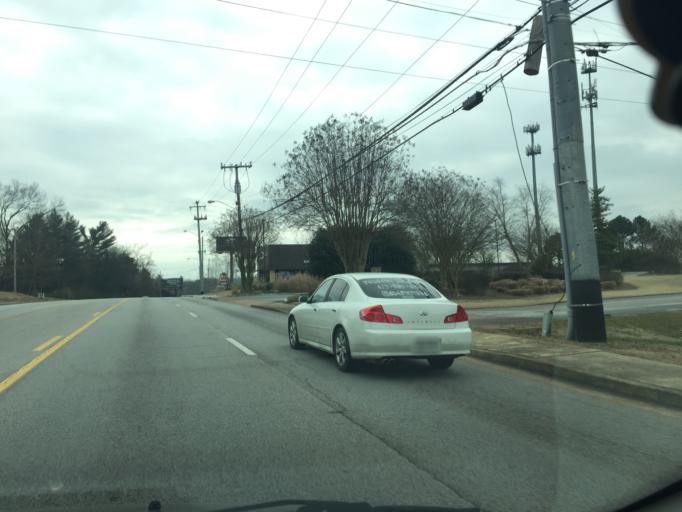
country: US
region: Tennessee
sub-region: Hamilton County
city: East Brainerd
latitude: 35.0108
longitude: -85.1553
